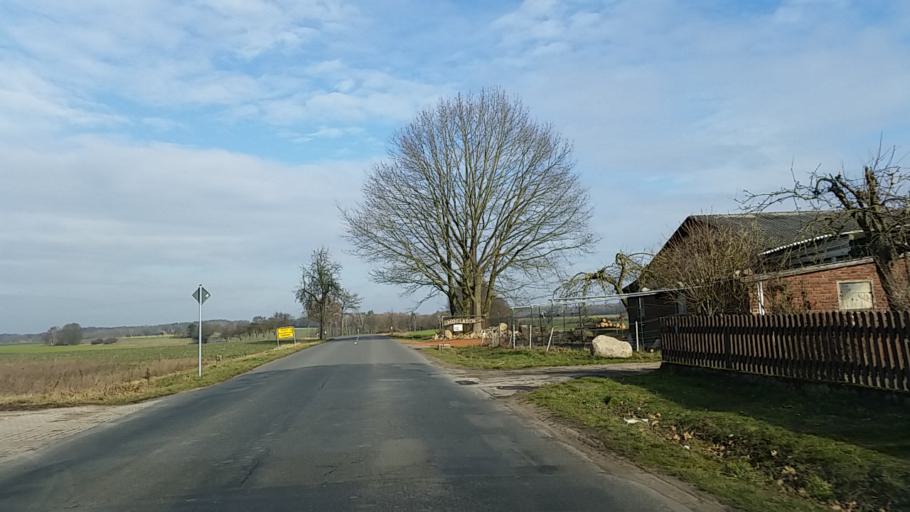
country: DE
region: Lower Saxony
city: Altenmedingen
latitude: 53.1499
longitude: 10.6189
